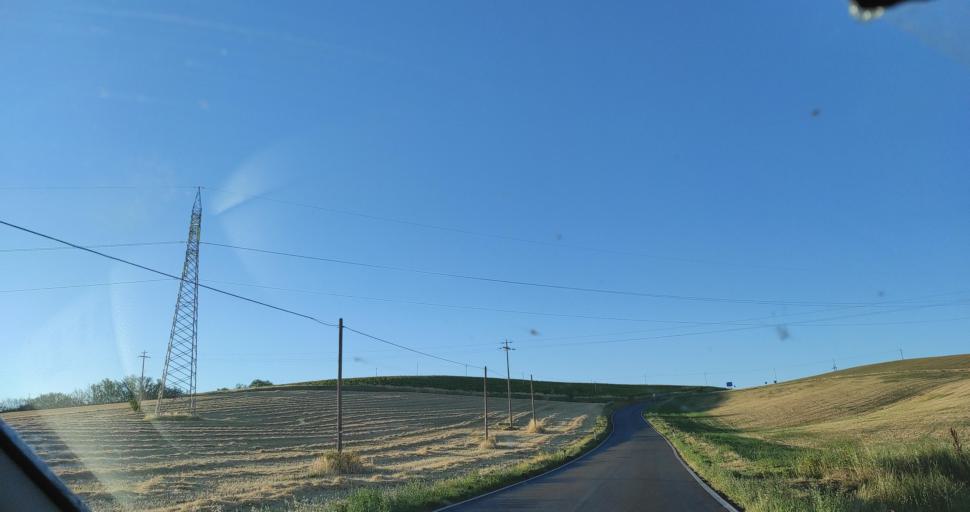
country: IT
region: The Marches
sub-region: Provincia di Macerata
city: Casette Verdini
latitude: 43.2318
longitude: 13.3940
